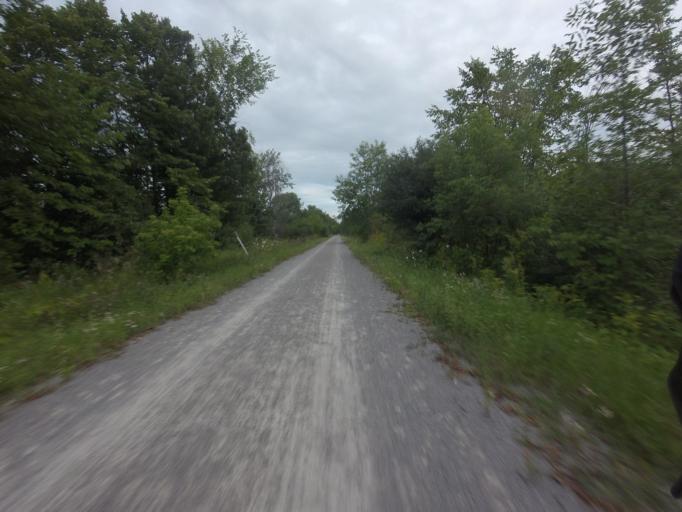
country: CA
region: Ontario
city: Carleton Place
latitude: 45.1445
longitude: -76.1160
